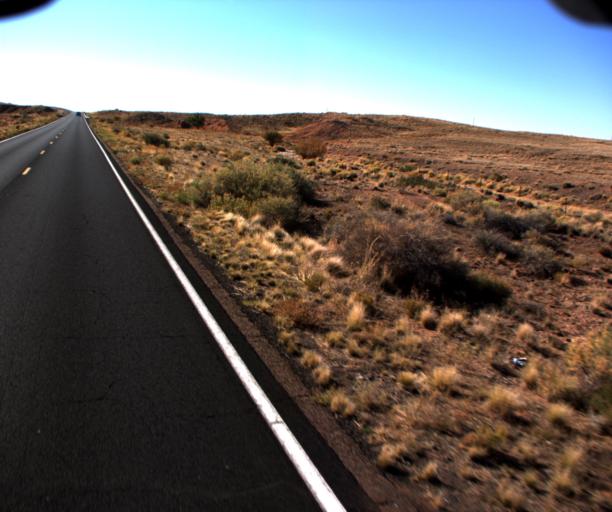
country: US
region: Arizona
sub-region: Navajo County
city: Dilkon
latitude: 35.3249
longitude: -110.4233
